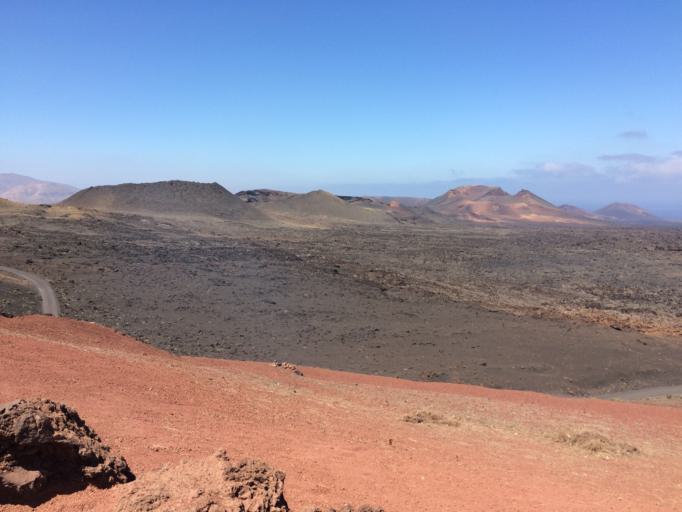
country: ES
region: Canary Islands
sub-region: Provincia de Las Palmas
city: Yaiza
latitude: 29.0057
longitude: -13.7533
